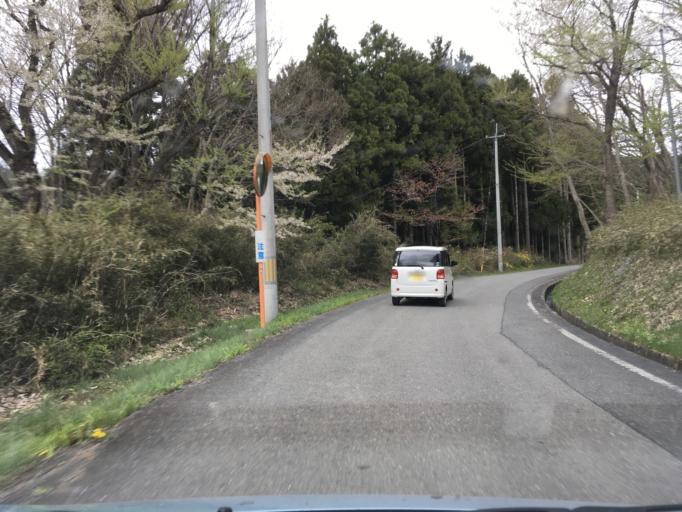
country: JP
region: Iwate
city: Ichinoseki
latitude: 38.9660
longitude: 141.1852
